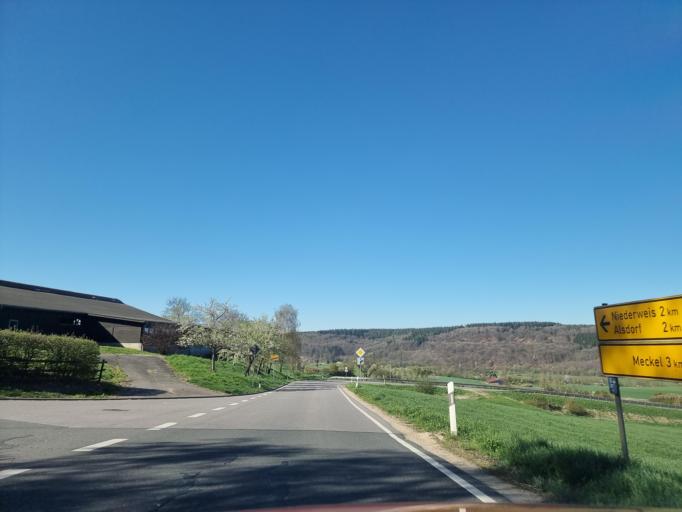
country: DE
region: Rheinland-Pfalz
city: Kaschenbach
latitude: 49.8768
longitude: 6.4794
